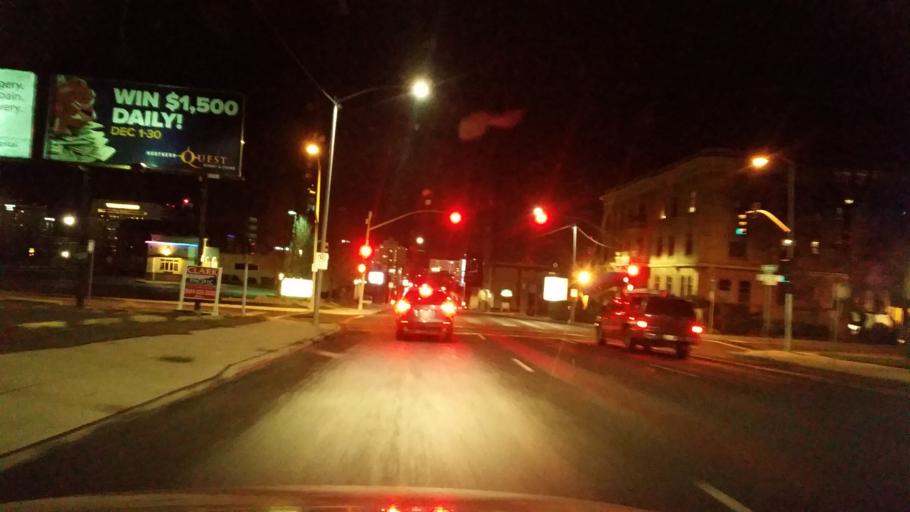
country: US
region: Washington
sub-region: Spokane County
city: Spokane
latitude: 47.6501
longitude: -117.4180
